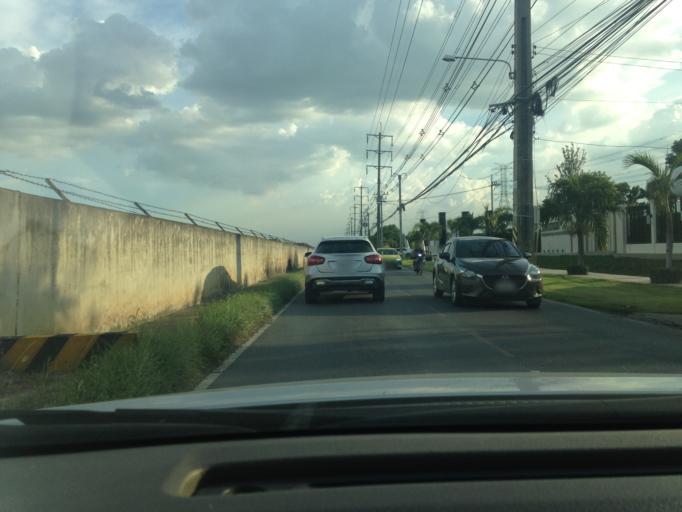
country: TH
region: Bangkok
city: Don Mueang
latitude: 13.9274
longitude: 100.5619
